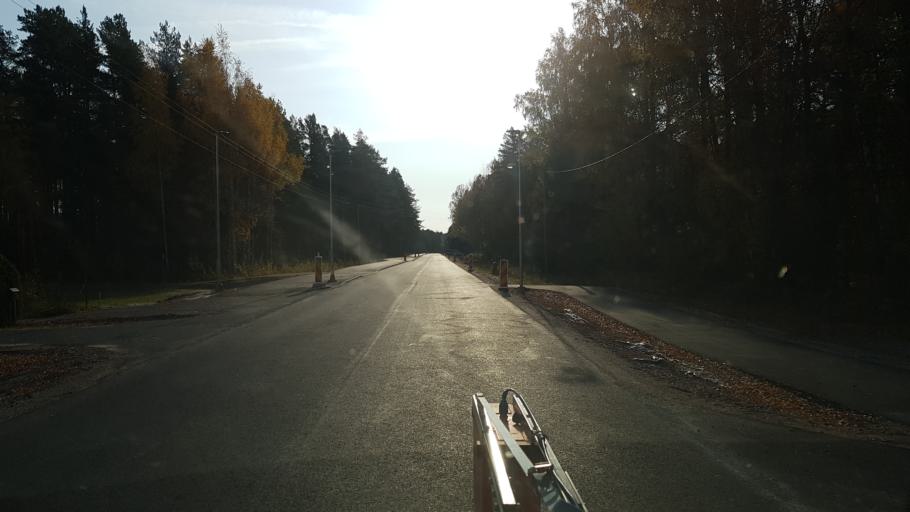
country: EE
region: Paernumaa
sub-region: Paikuse vald
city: Paikuse
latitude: 58.3587
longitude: 24.6120
